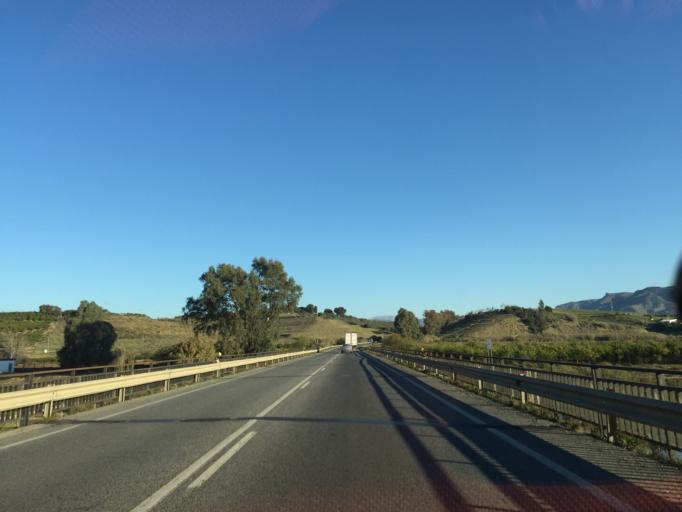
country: ES
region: Andalusia
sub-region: Provincia de Malaga
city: Pizarra
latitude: 36.7227
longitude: -4.7086
